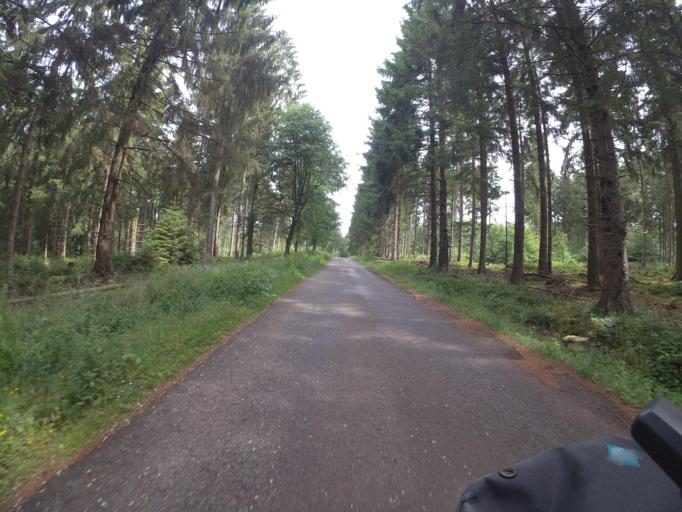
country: DE
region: North Rhine-Westphalia
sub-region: Regierungsbezirk Koln
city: Hurtgenwald
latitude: 50.7391
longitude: 6.3844
